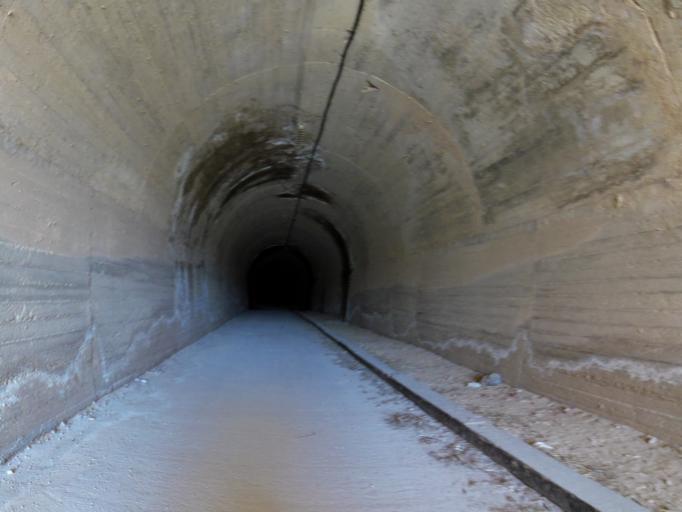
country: ES
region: Valencia
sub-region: Provincia de Alicante
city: Agost
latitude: 38.4839
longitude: -0.6238
